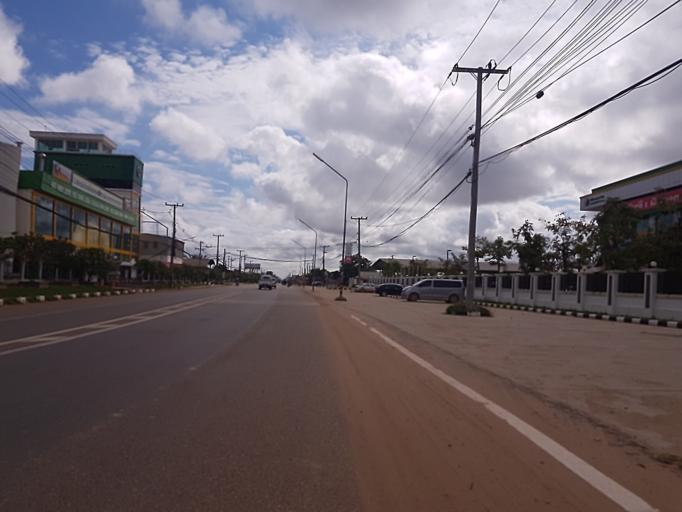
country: TH
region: Nong Khai
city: Tha Bo
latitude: 17.8705
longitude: 102.6556
